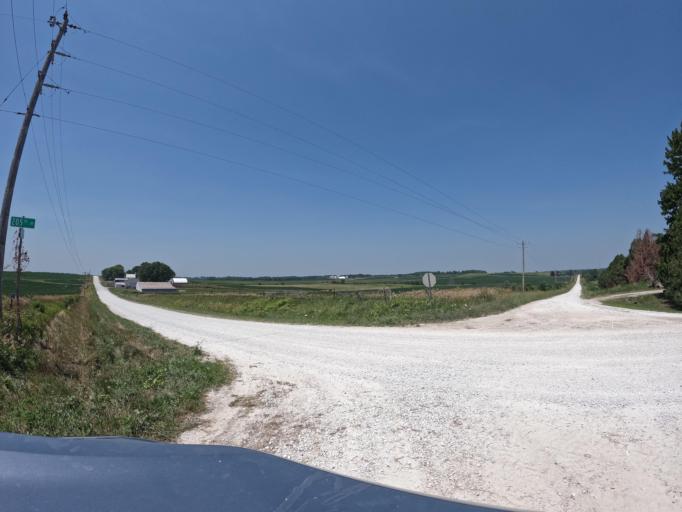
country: US
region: Iowa
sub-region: Keokuk County
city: Sigourney
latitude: 41.2866
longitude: -92.2097
